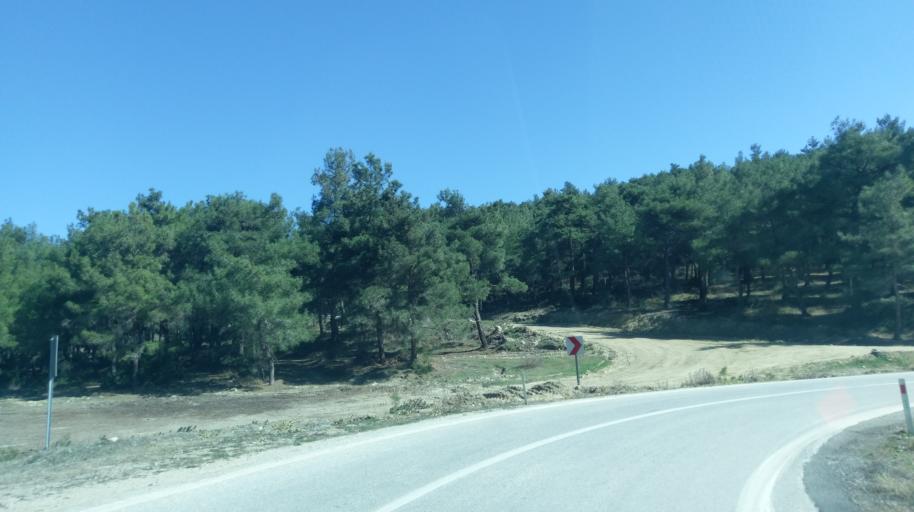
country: TR
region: Canakkale
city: Eceabat
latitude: 40.1244
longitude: 26.2953
